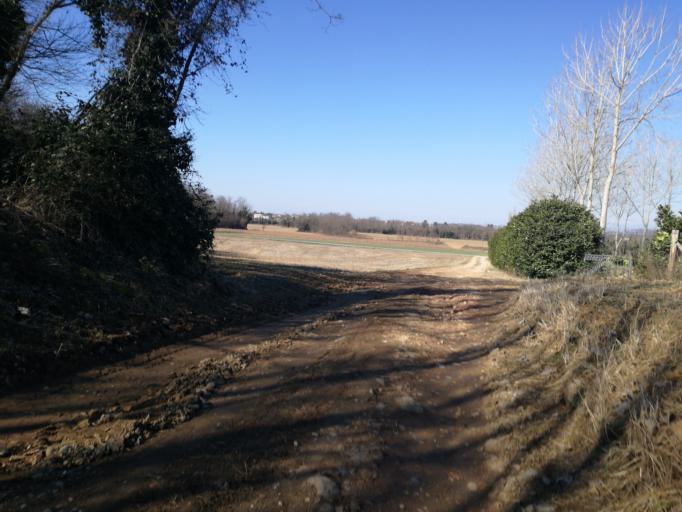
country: IT
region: Lombardy
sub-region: Provincia di Lecco
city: Verderio Inferiore
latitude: 45.6545
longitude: 9.4313
